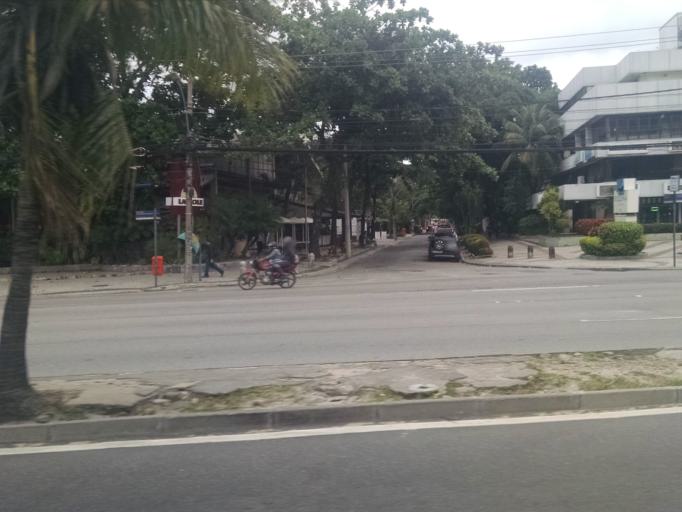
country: BR
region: Rio de Janeiro
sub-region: Rio De Janeiro
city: Rio de Janeiro
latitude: -23.0072
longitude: -43.3065
